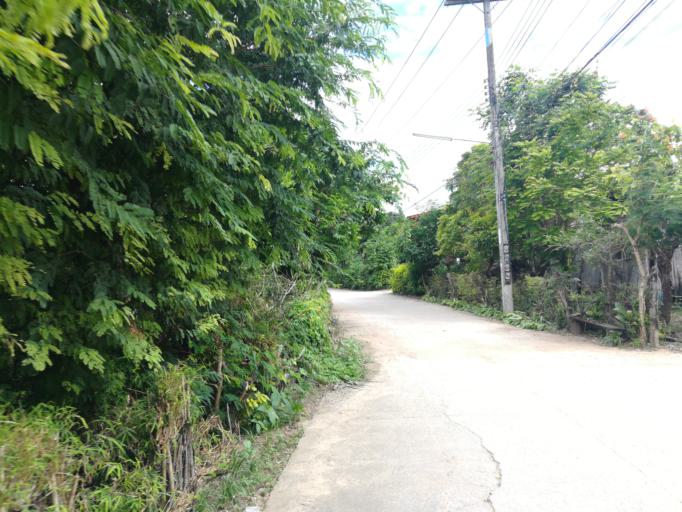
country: TH
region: Chiang Mai
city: Chom Thong
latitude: 18.4060
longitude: 98.6497
